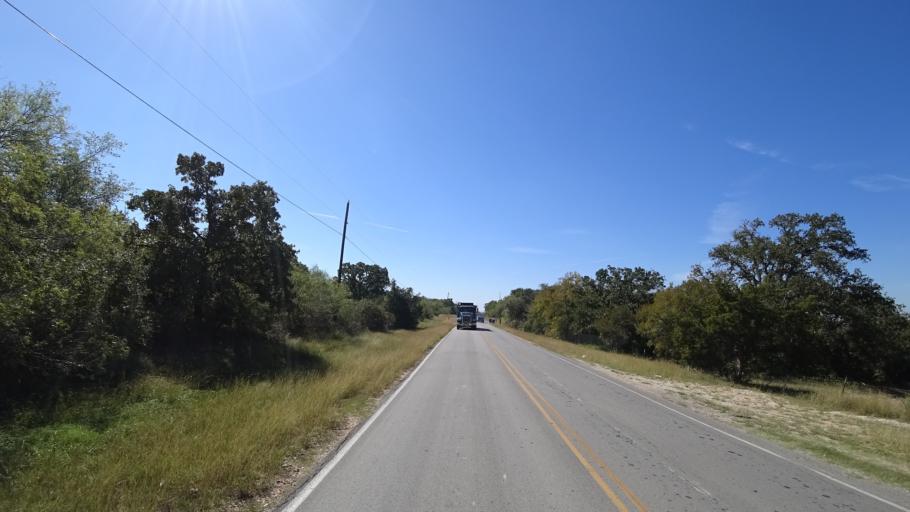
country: US
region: Texas
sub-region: Travis County
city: Hornsby Bend
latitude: 30.2741
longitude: -97.6140
